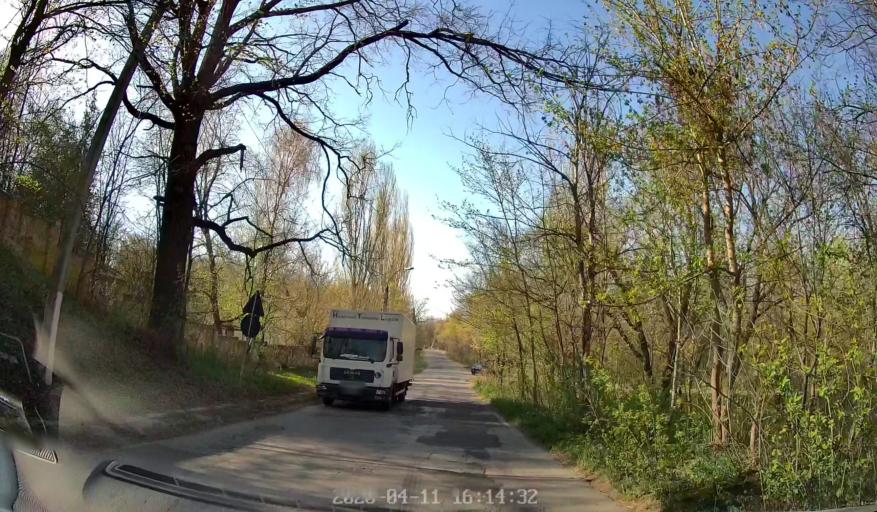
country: MD
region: Chisinau
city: Vadul lui Voda
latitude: 47.0758
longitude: 29.1004
